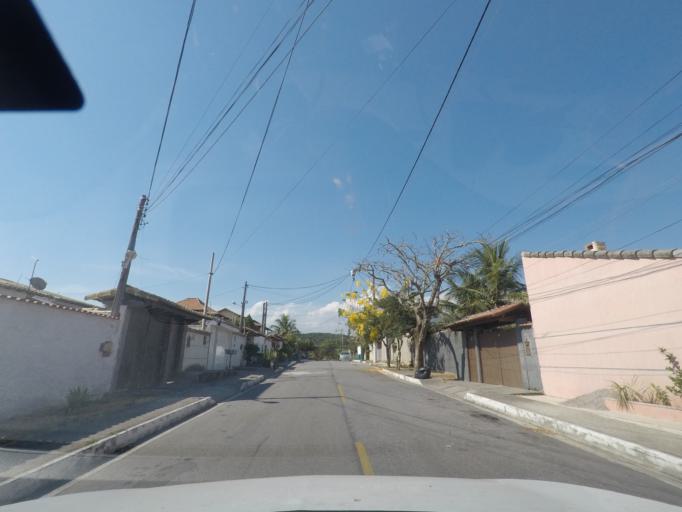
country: BR
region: Rio de Janeiro
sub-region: Niteroi
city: Niteroi
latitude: -22.9659
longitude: -42.9747
